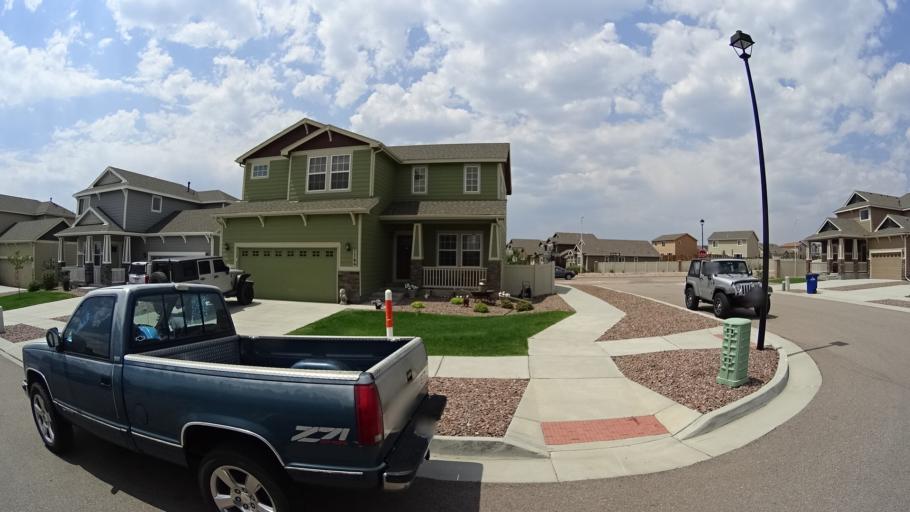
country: US
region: Colorado
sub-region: El Paso County
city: Black Forest
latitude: 38.9458
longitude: -104.6968
